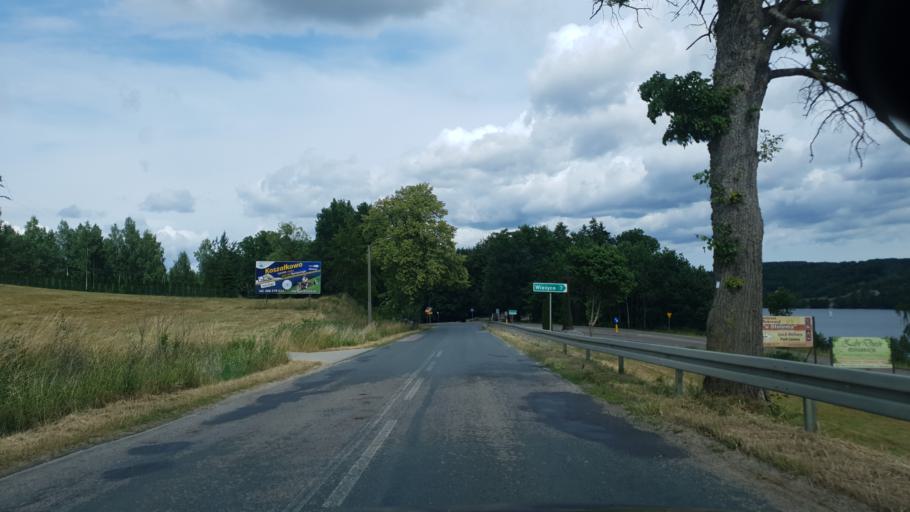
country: PL
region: Pomeranian Voivodeship
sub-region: Powiat kartuski
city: Chmielno
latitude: 54.2738
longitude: 18.0926
